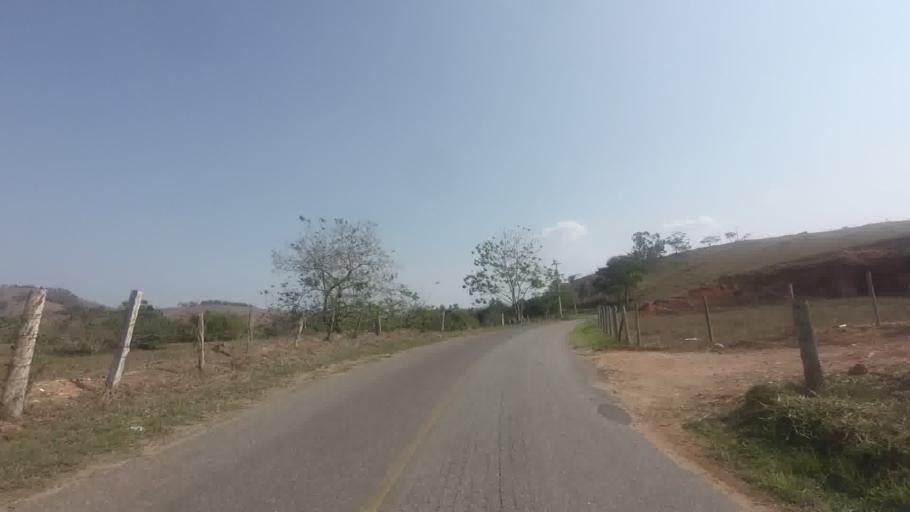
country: BR
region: Rio de Janeiro
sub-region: Bom Jesus Do Itabapoana
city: Bom Jesus do Itabapoana
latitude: -21.1379
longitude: -41.5677
